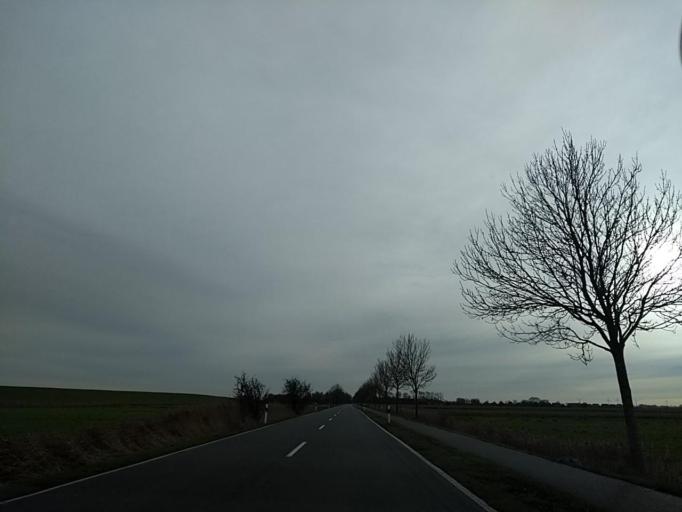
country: DE
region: Lower Saxony
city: Jemgum
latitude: 53.3011
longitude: 7.3444
